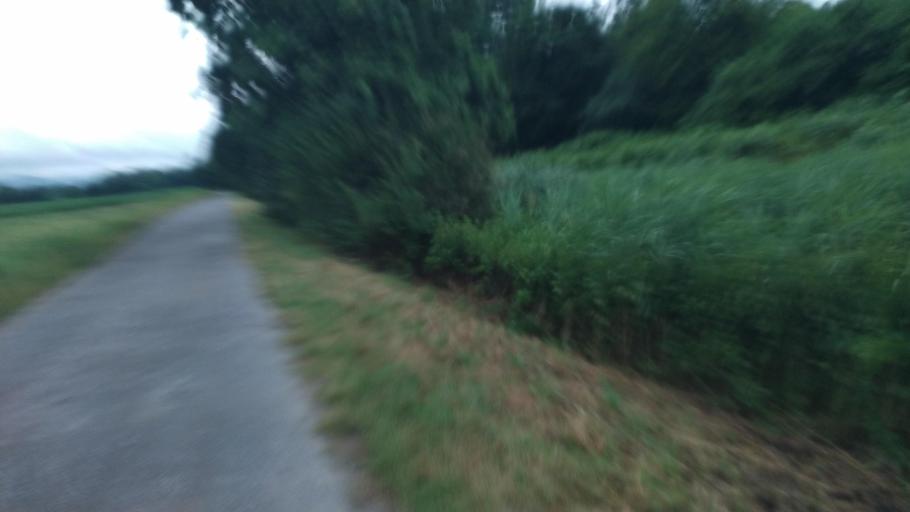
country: DE
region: Baden-Wuerttemberg
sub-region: Karlsruhe Region
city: Ettlingen
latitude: 48.9666
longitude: 8.3830
